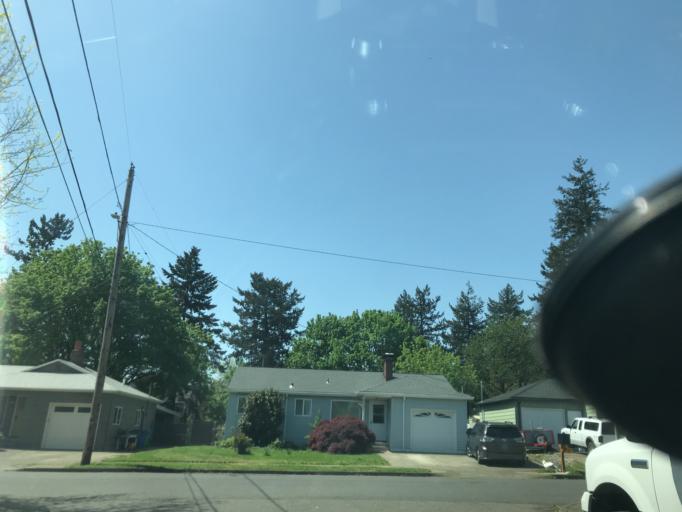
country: US
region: Oregon
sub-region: Multnomah County
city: Lents
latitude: 45.4916
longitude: -122.5581
